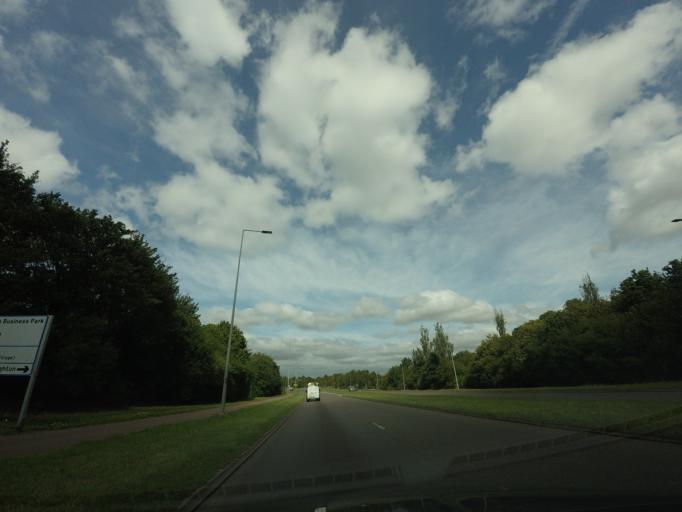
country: GB
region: England
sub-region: Milton Keynes
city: Broughton
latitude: 52.0430
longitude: -0.6960
